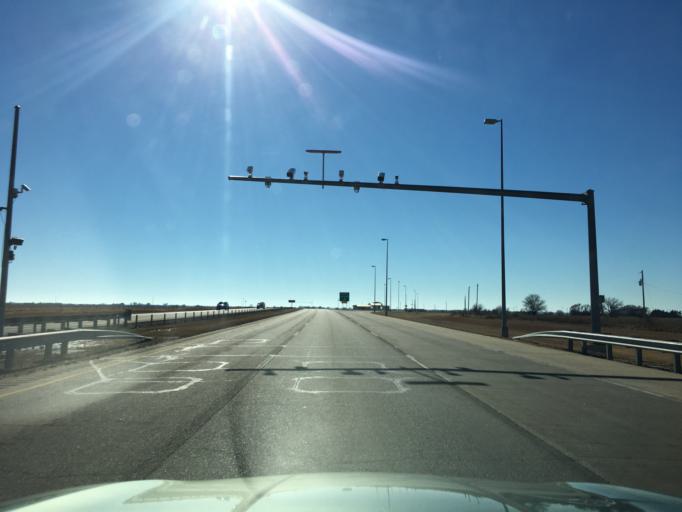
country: US
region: Oklahoma
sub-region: Kay County
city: Blackwell
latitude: 36.9908
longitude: -97.3450
